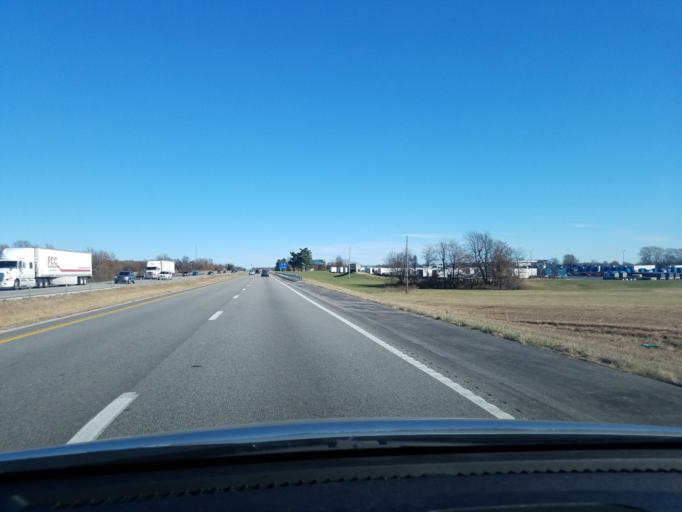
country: US
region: Missouri
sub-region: Greene County
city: Strafford
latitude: 37.2598
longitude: -93.1550
